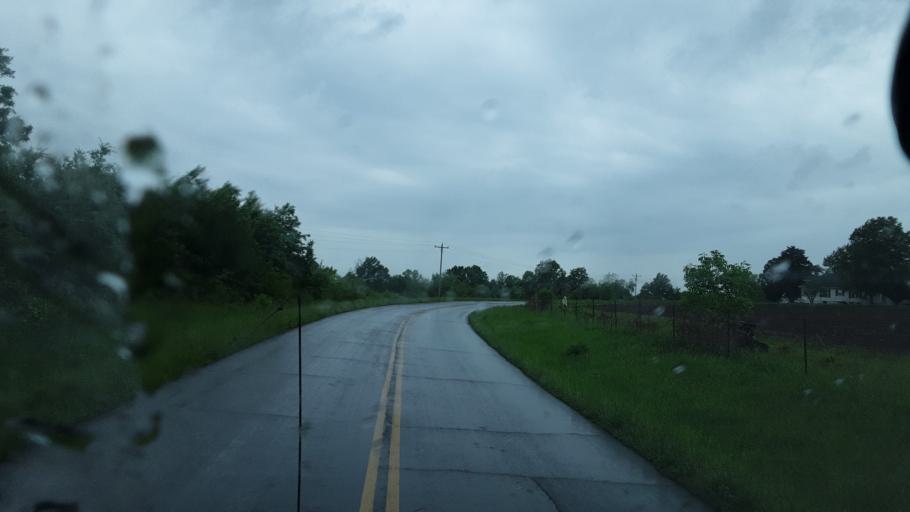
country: US
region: Missouri
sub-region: Boone County
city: Centralia
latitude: 39.3886
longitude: -92.2212
